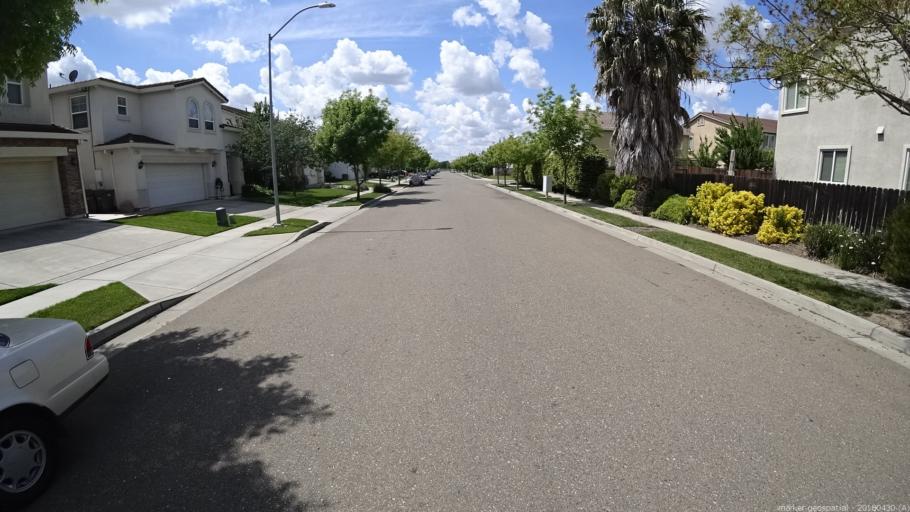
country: US
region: California
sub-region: Yolo County
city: West Sacramento
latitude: 38.5490
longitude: -121.5286
